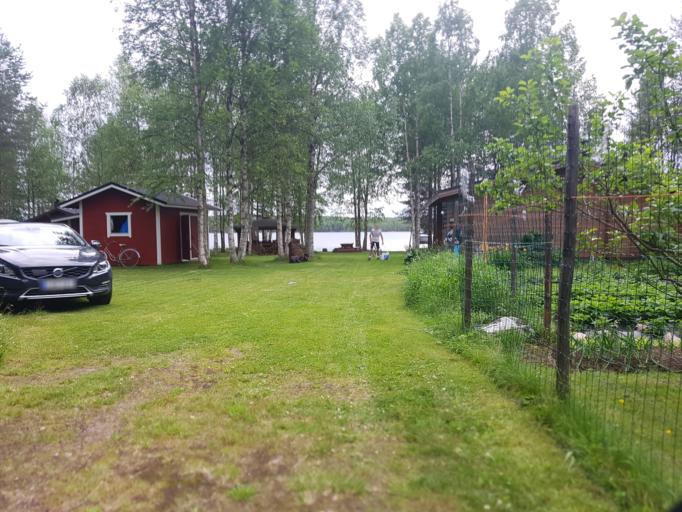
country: FI
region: Kainuu
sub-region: Kehys-Kainuu
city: Kuhmo
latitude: 64.4502
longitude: 29.7218
